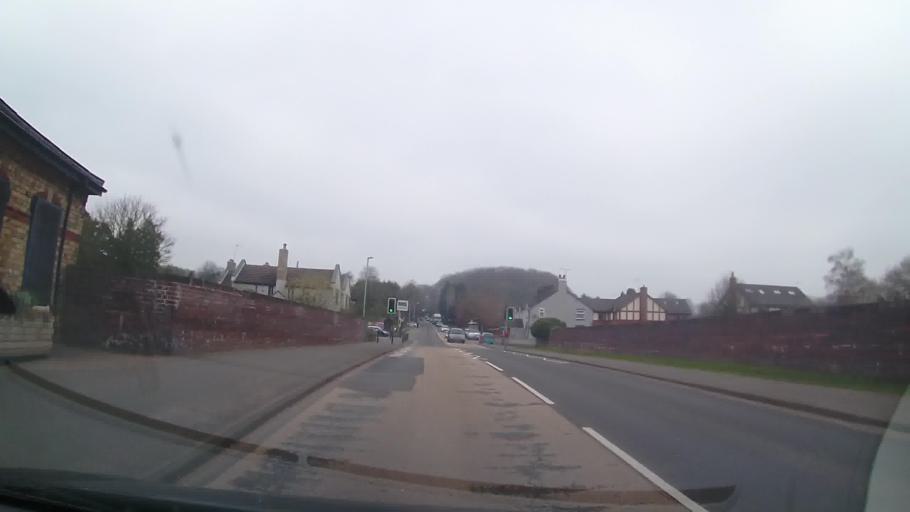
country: GB
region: England
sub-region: Staffordshire
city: Standon
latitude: 52.9600
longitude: -2.3050
